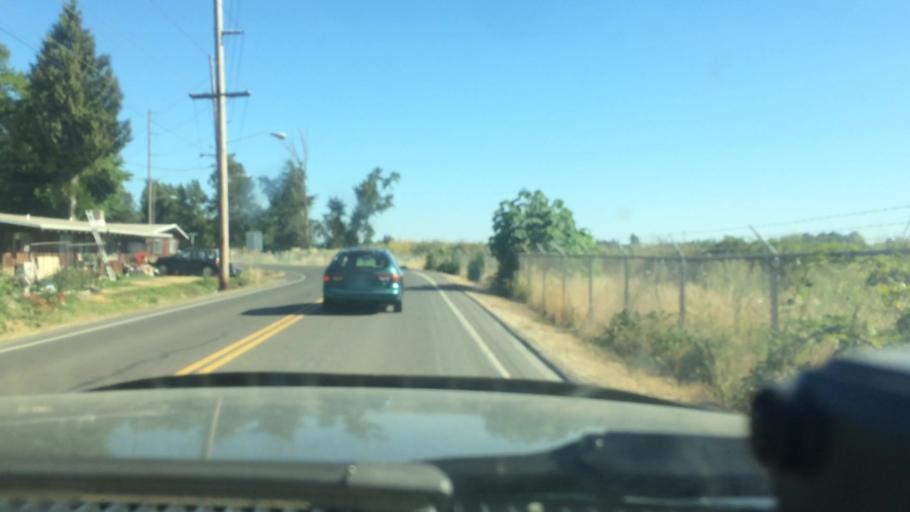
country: US
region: Oregon
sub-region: Lane County
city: Eugene
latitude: 44.1004
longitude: -123.1142
